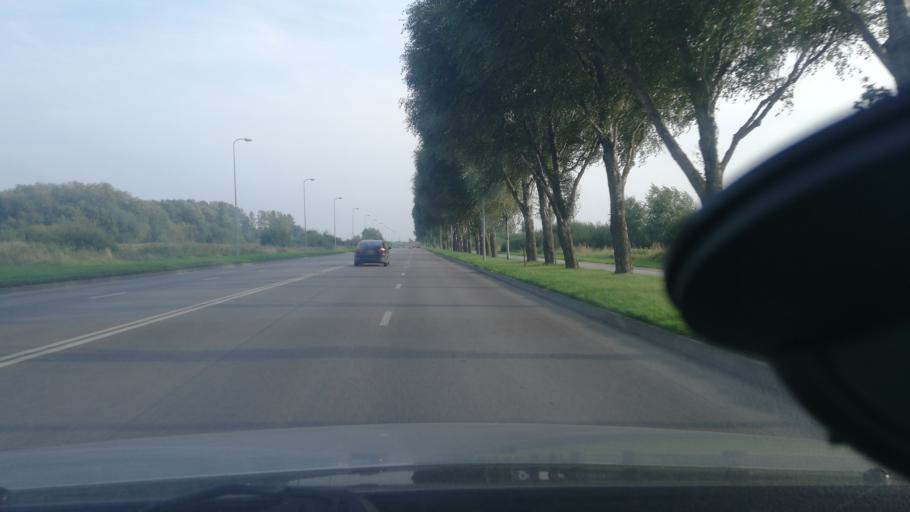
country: LT
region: Klaipedos apskritis
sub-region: Klaipeda
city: Klaipeda
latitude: 55.6600
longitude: 21.1679
